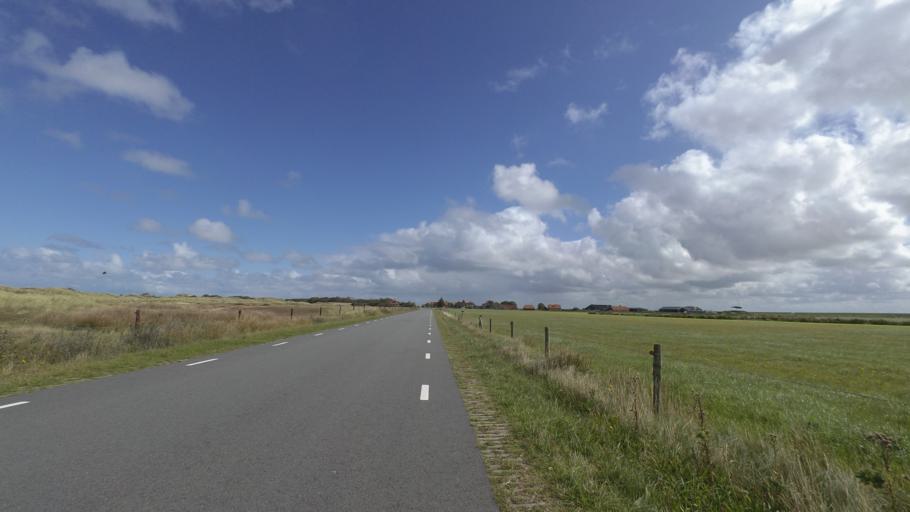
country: NL
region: Friesland
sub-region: Gemeente Ameland
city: Nes
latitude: 53.4502
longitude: 5.8310
